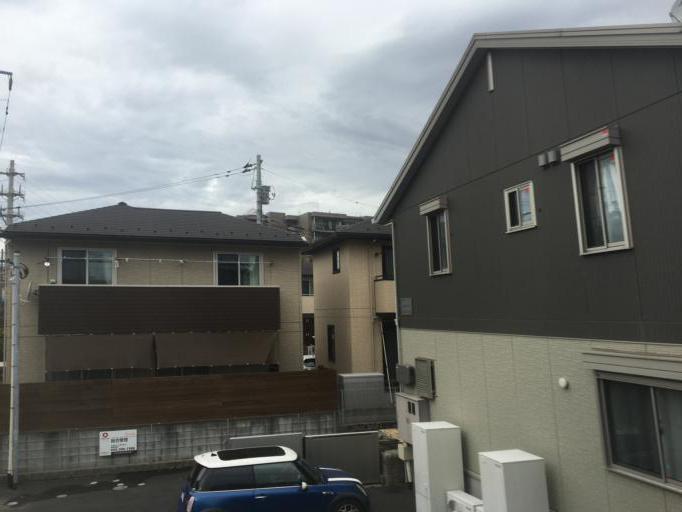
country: JP
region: Chiba
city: Funabashi
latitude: 35.6858
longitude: 140.0439
